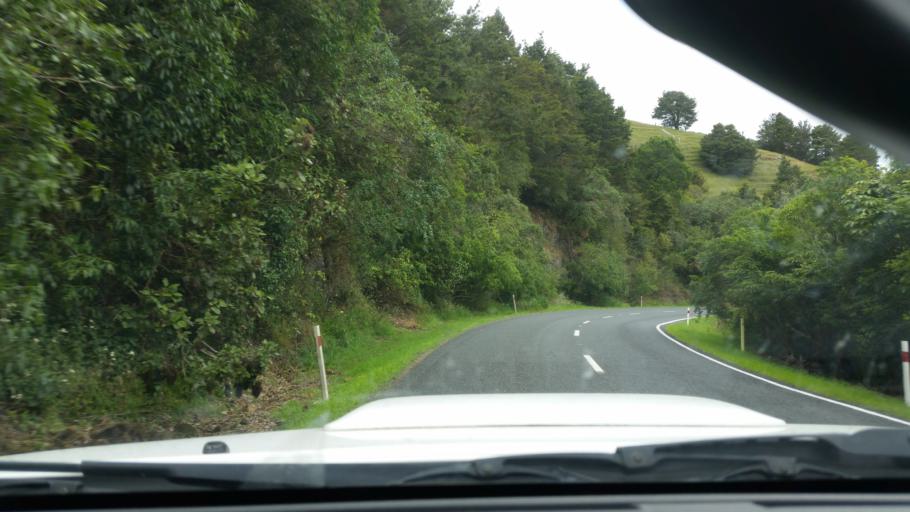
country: NZ
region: Northland
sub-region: Kaipara District
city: Dargaville
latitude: -35.7642
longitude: 173.9058
